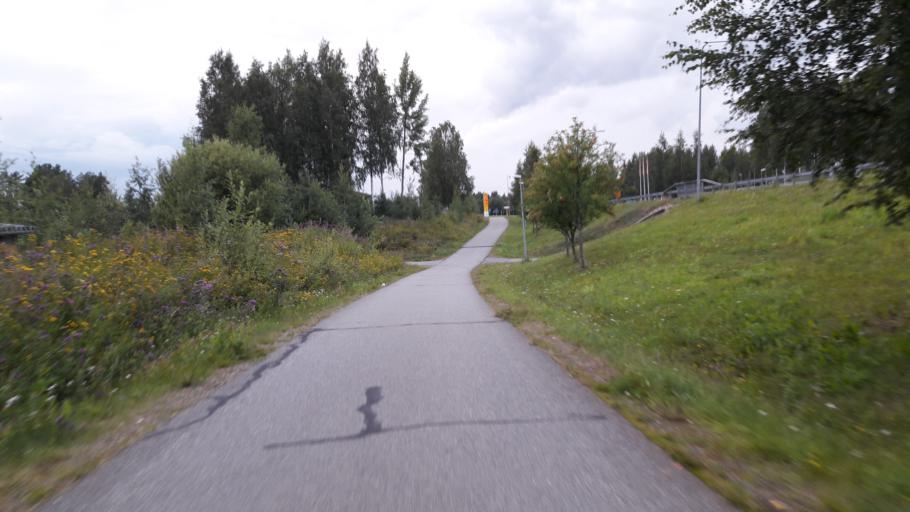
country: FI
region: North Karelia
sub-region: Joensuu
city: Joensuu
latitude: 62.5410
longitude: 29.8437
